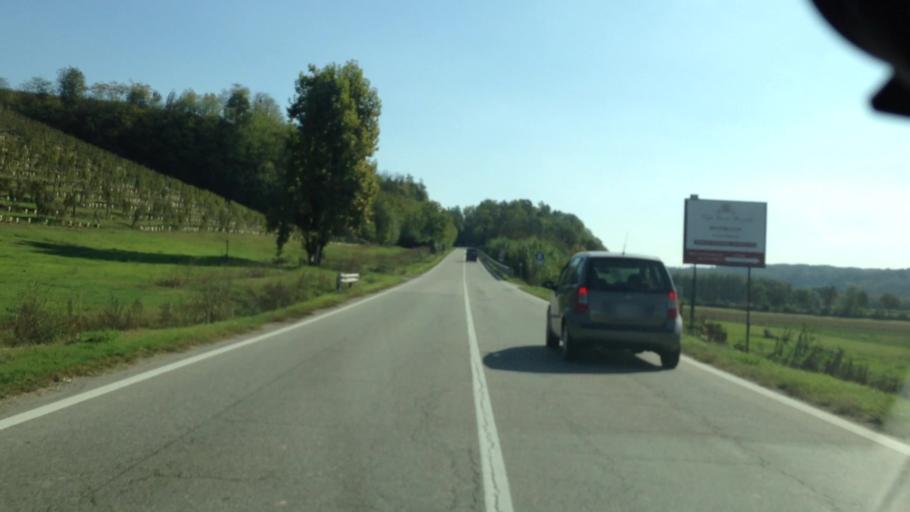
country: IT
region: Piedmont
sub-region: Provincia di Asti
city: Castello di Annone
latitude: 44.8939
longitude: 8.2996
